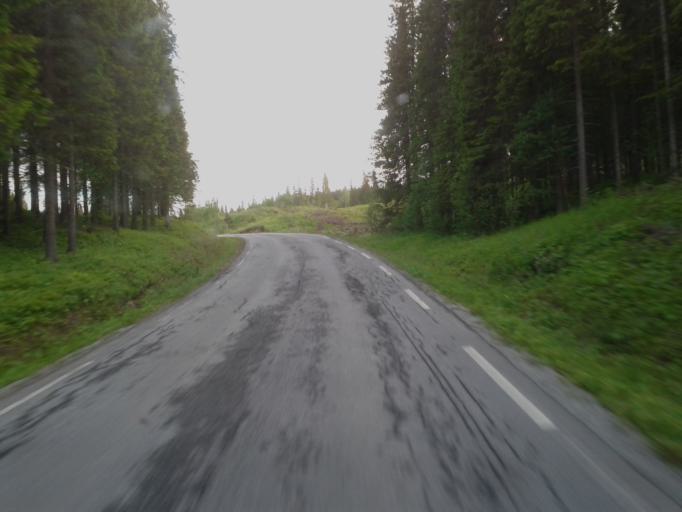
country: NO
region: Nordland
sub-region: Grane
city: Trofors
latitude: 65.5003
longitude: 13.6716
